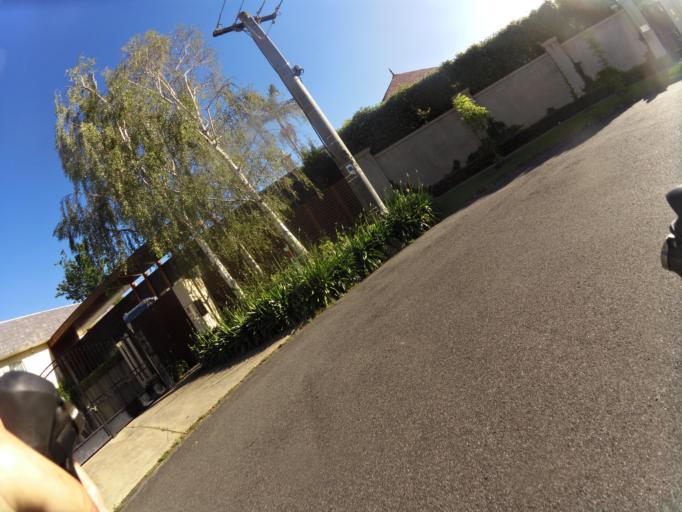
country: AU
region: Victoria
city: Toorak
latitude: -37.8448
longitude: 145.0184
